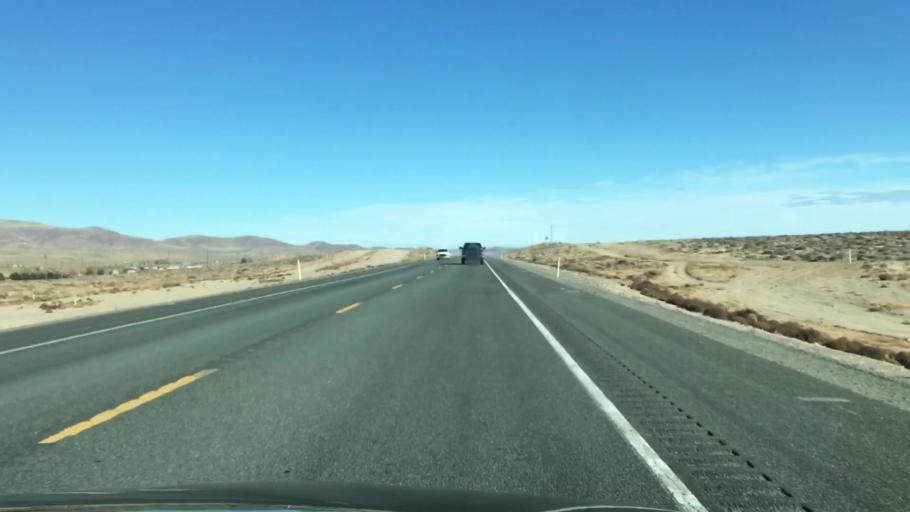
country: US
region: Nevada
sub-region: Lyon County
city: Stagecoach
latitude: 39.3796
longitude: -119.3249
